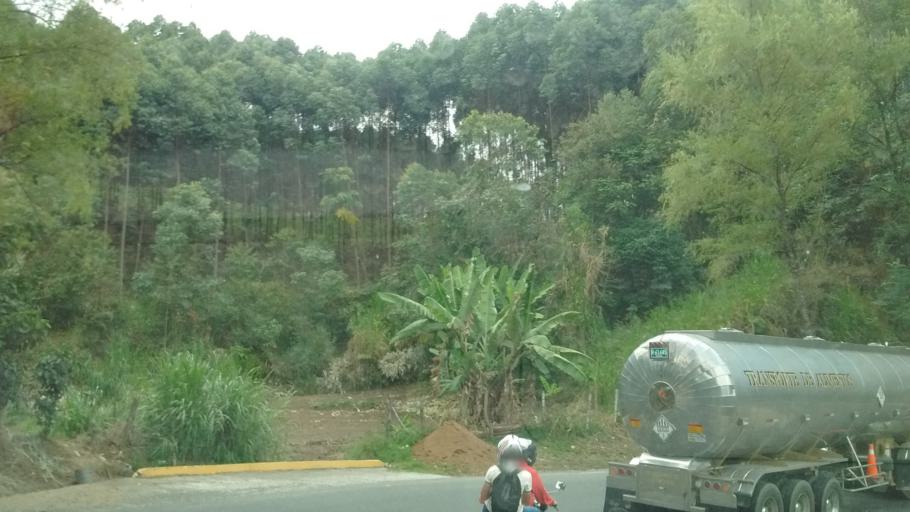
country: CO
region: Cauca
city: Rosas
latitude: 2.3080
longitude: -76.6842
